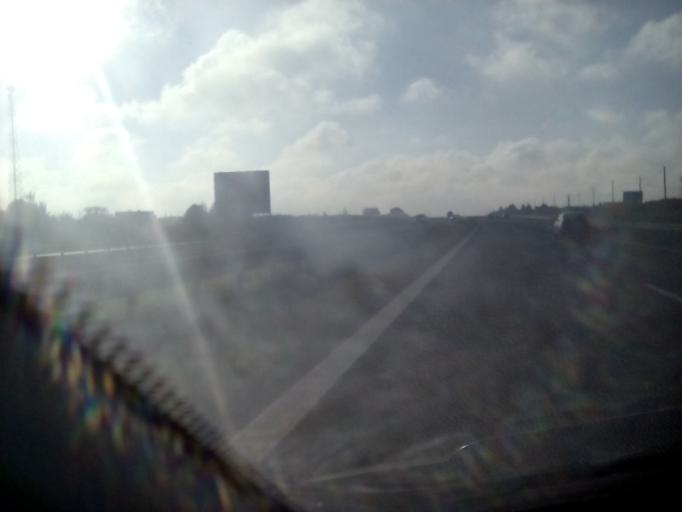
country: PL
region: Masovian Voivodeship
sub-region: Powiat grojecki
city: Jasieniec
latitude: 51.7789
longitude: 20.8965
